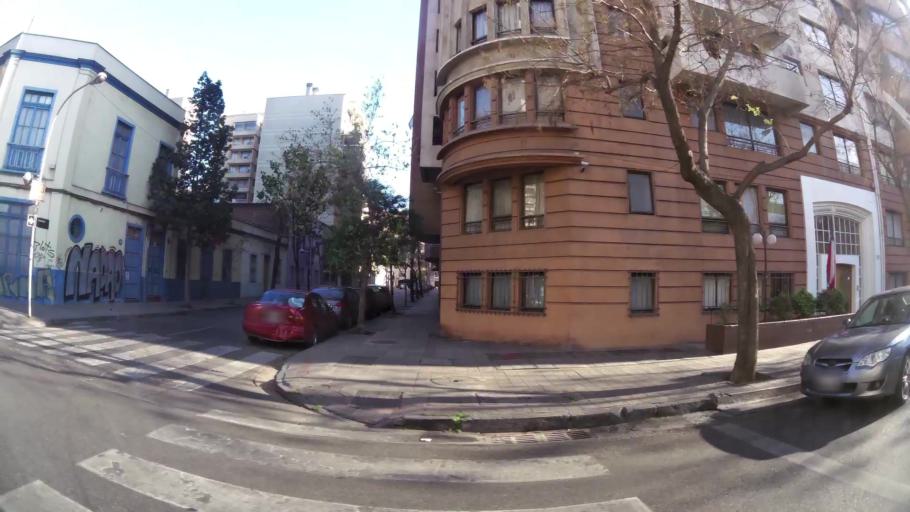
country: CL
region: Santiago Metropolitan
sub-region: Provincia de Santiago
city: Santiago
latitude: -33.4466
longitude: -70.6385
